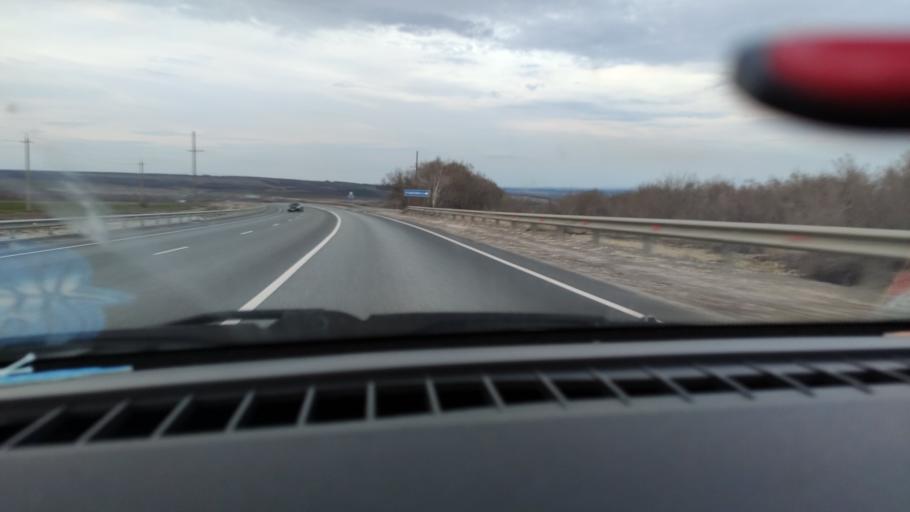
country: RU
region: Saratov
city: Sinodskoye
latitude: 51.9075
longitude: 46.5505
